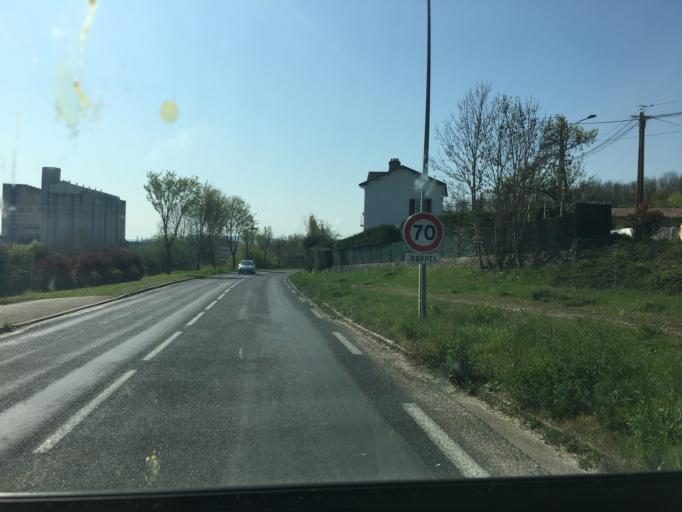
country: FR
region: Lorraine
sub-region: Departement de Meurthe-et-Moselle
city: Norroy-les-Pont-a-Mousson
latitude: 48.9228
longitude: 6.0381
